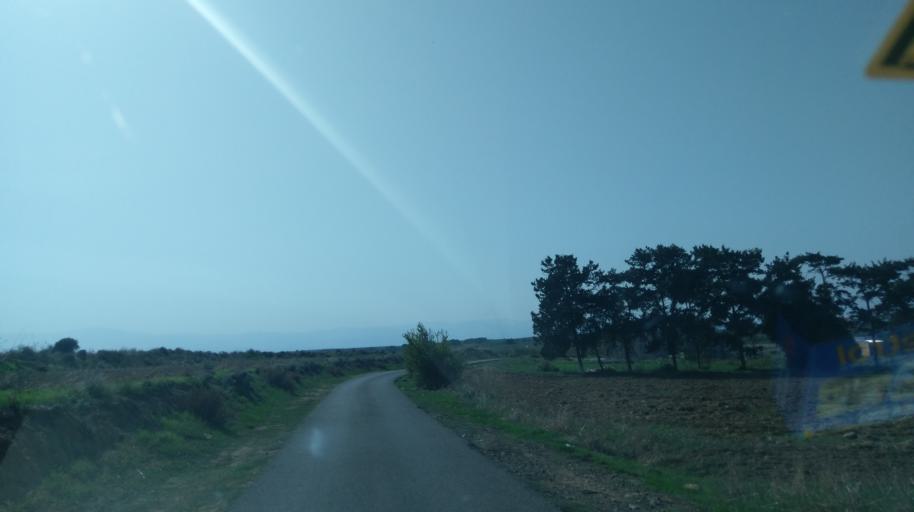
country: CY
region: Lefkosia
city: Morfou
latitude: 35.2969
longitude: 32.9590
